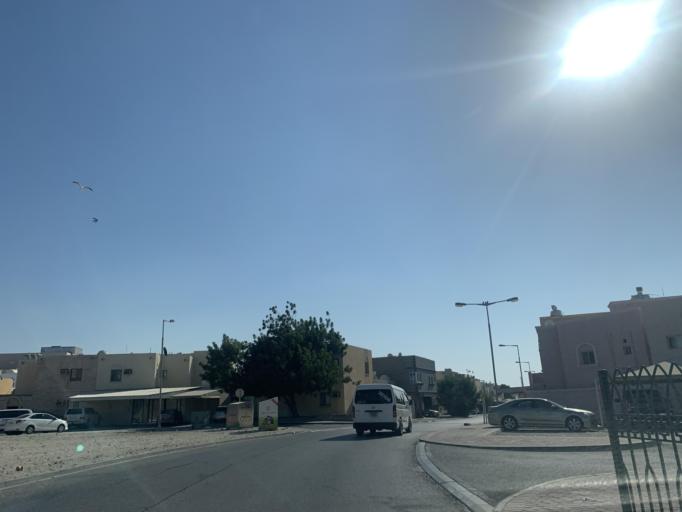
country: BH
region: Central Governorate
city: Madinat Hamad
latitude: 26.1119
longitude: 50.5096
